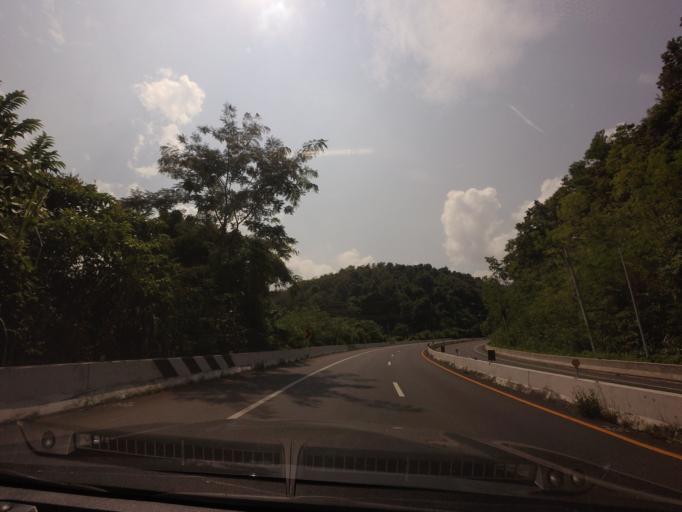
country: TH
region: Phrae
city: Den Chai
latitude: 17.8732
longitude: 100.0462
